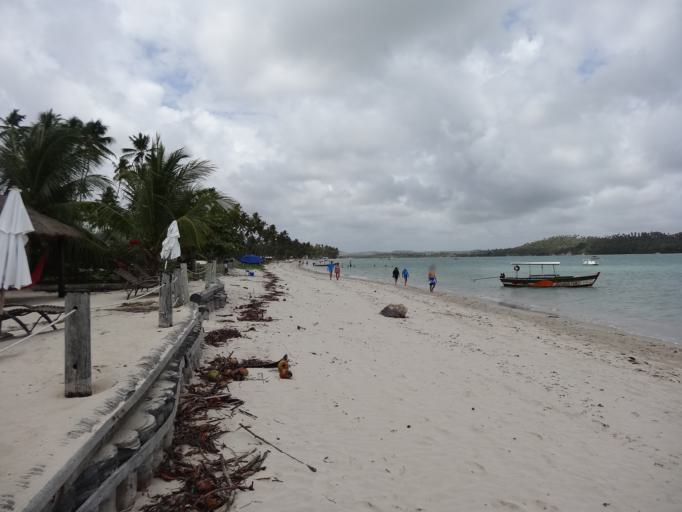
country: BR
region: Pernambuco
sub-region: Tamandare
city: Tamandare
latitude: -8.6994
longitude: -35.0850
